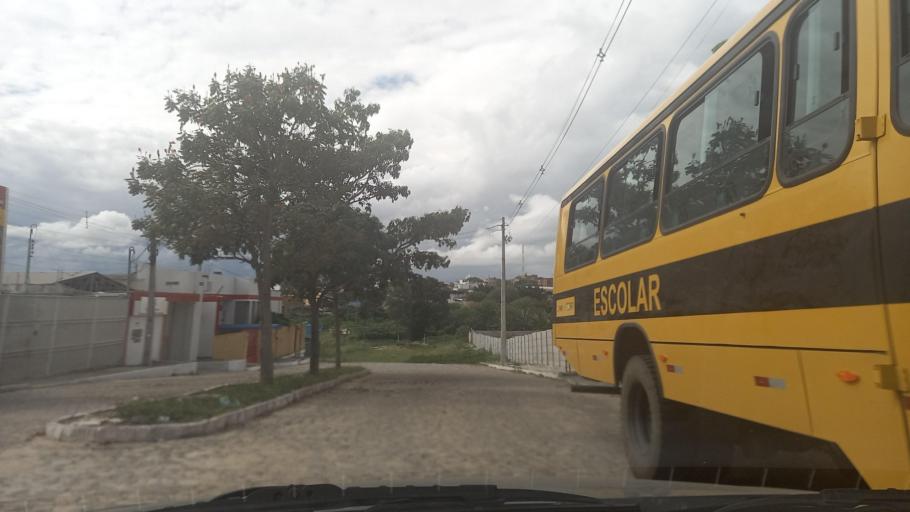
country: BR
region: Pernambuco
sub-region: Caruaru
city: Caruaru
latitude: -8.2916
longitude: -35.9874
